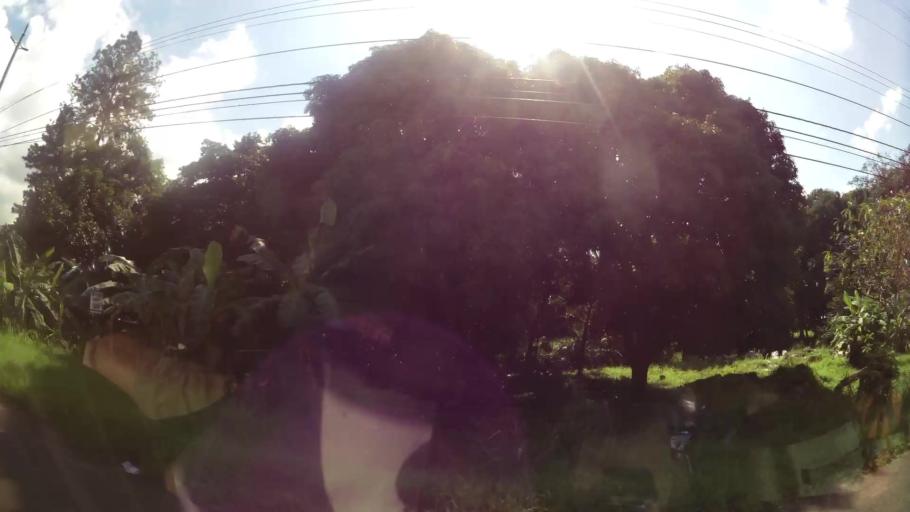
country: PA
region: Panama
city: Nuevo Arraijan
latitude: 8.9079
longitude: -79.7463
